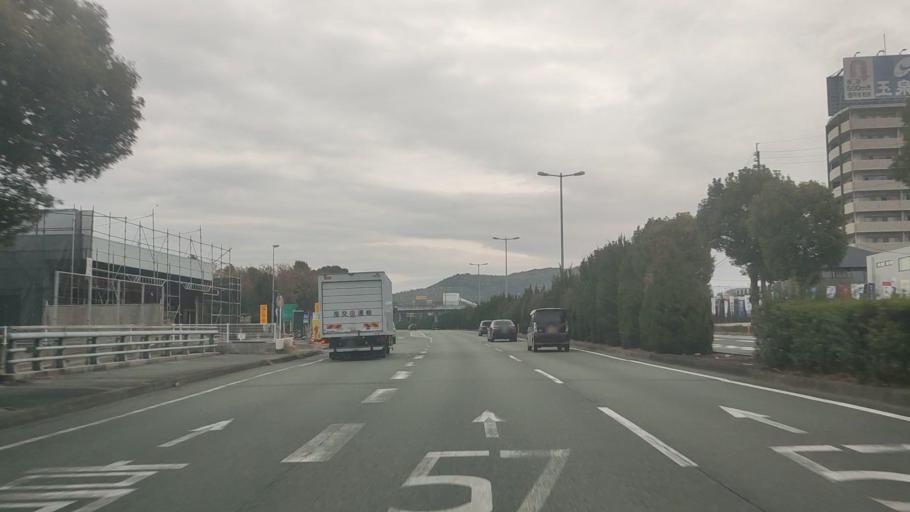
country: JP
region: Kumamoto
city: Kumamoto
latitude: 32.8320
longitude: 130.7736
